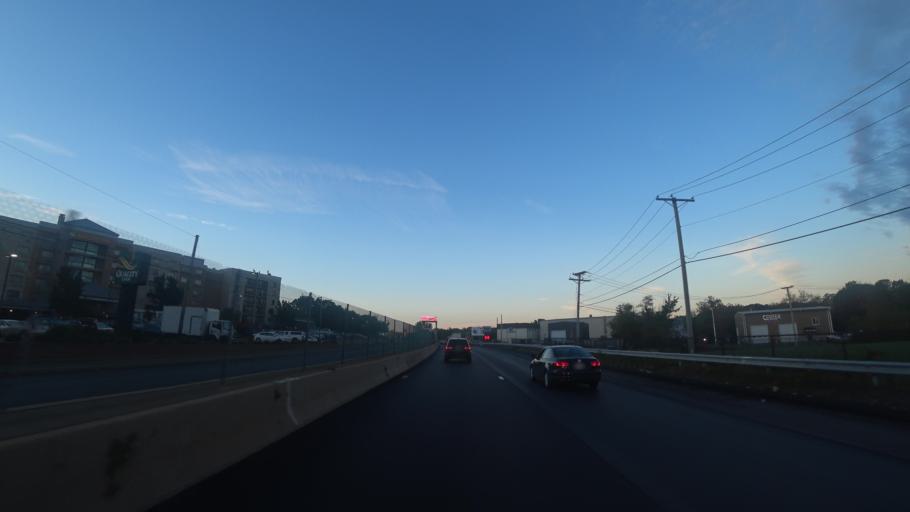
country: US
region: Massachusetts
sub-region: Essex County
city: Saugus
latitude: 42.4468
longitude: -71.0247
